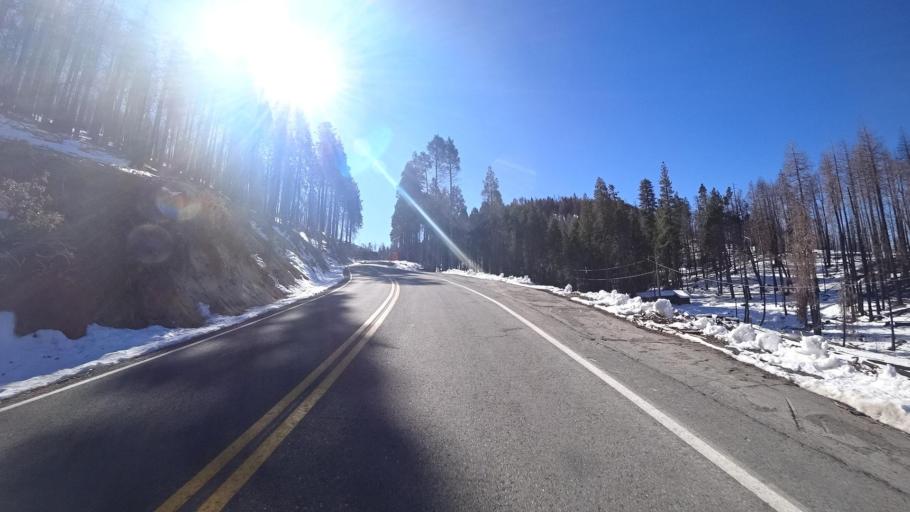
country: US
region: California
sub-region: Kern County
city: Alta Sierra
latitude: 35.7428
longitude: -118.5570
